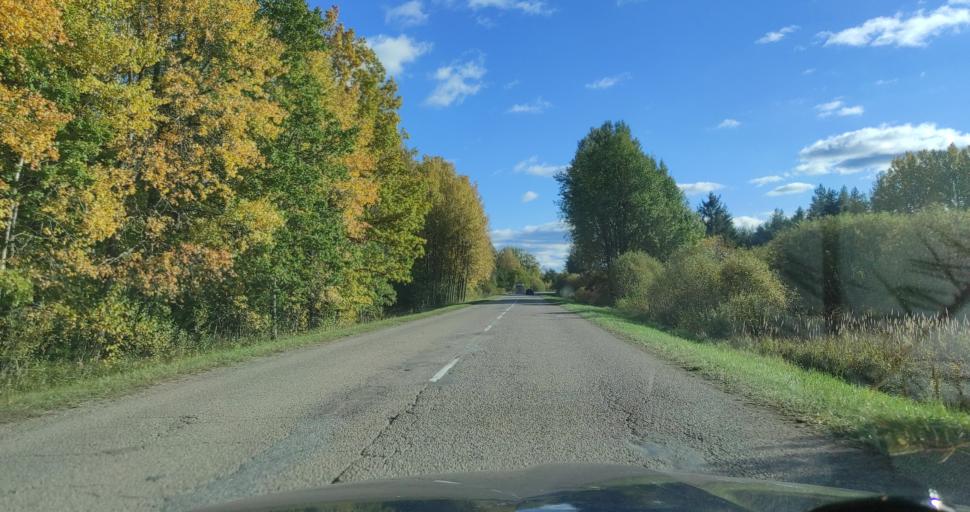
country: LV
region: Aizpute
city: Aizpute
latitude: 56.7904
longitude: 21.5105
